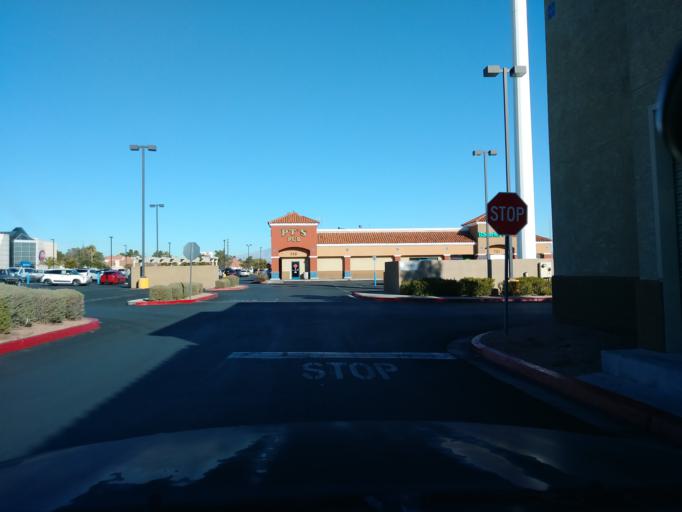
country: US
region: Nevada
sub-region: Clark County
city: Spring Valley
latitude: 36.1645
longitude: -115.2449
